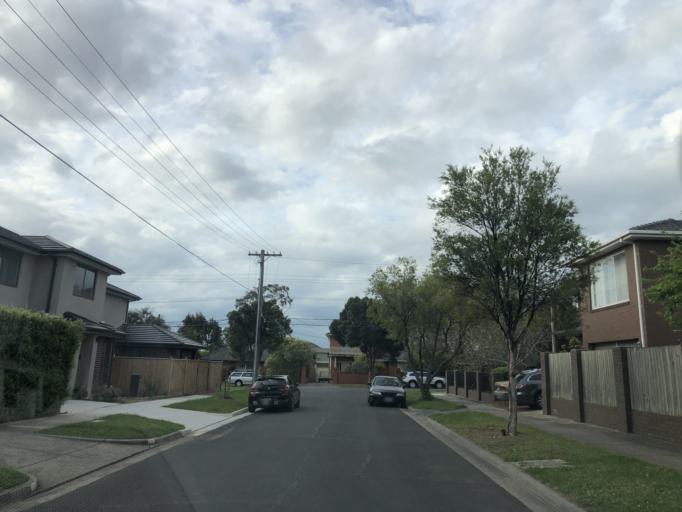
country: AU
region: Victoria
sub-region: Monash
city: Ashwood
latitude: -37.8637
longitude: 145.1183
